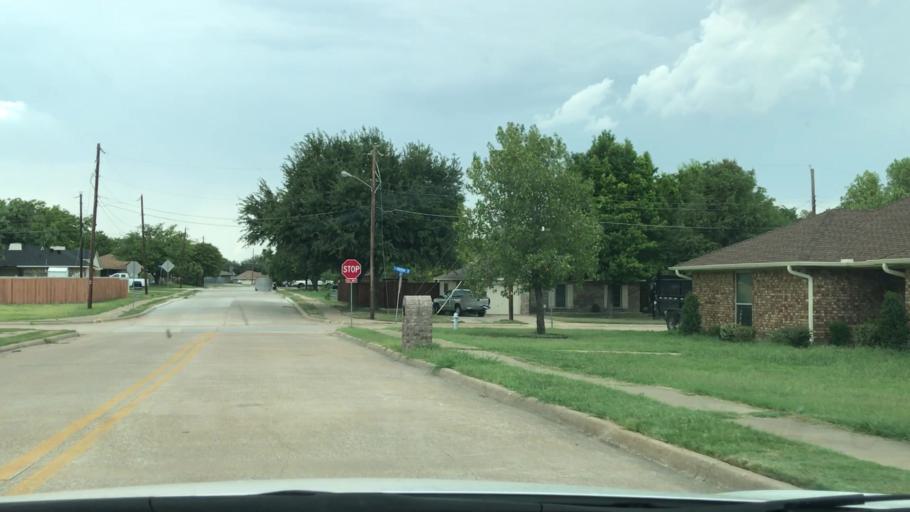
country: US
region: Texas
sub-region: Dallas County
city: Sachse
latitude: 32.9769
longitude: -96.5833
